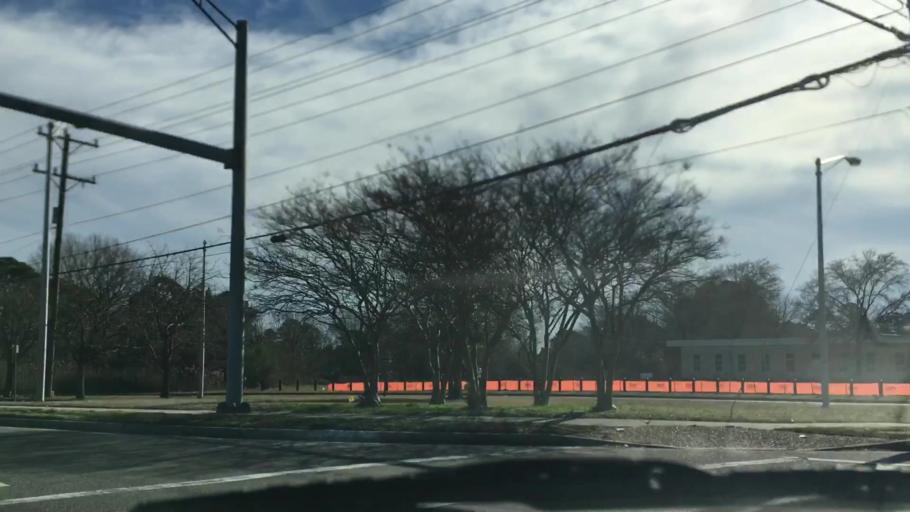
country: US
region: Virginia
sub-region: City of Norfolk
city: Norfolk
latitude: 36.8559
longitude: -76.2322
